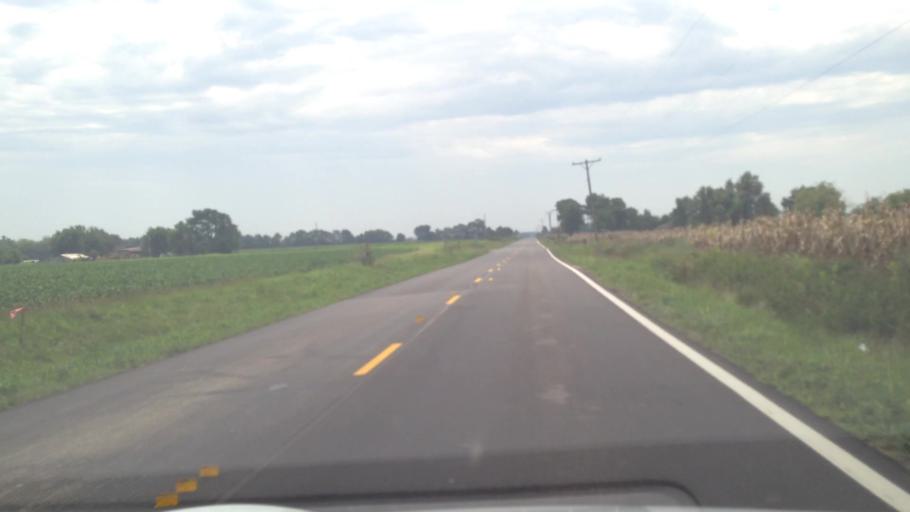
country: US
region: Kansas
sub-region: Crawford County
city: Girard
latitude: 37.6322
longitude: -94.9698
